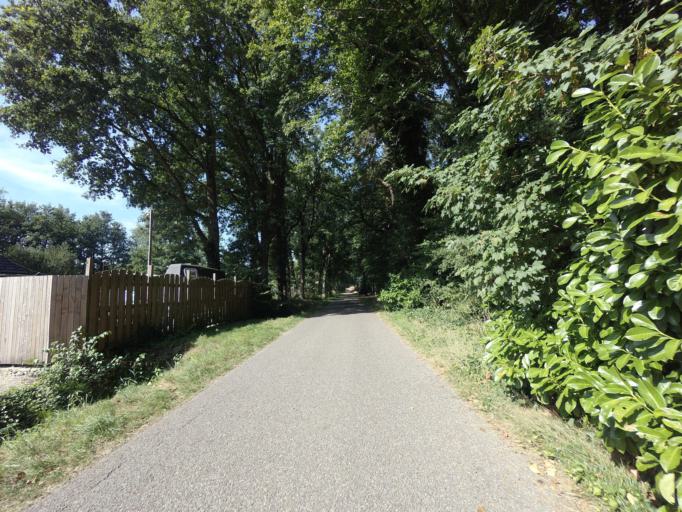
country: NL
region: Gelderland
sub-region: Gemeente Apeldoorn
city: Loenen
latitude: 52.1299
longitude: 6.0320
